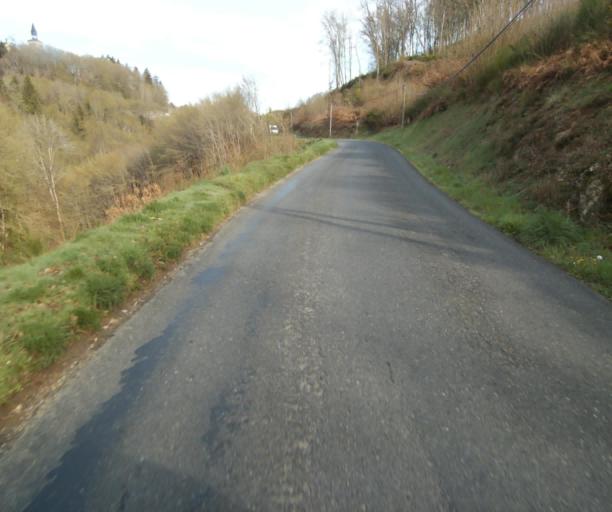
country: FR
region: Limousin
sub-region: Departement de la Correze
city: Naves
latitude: 45.3439
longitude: 1.8193
